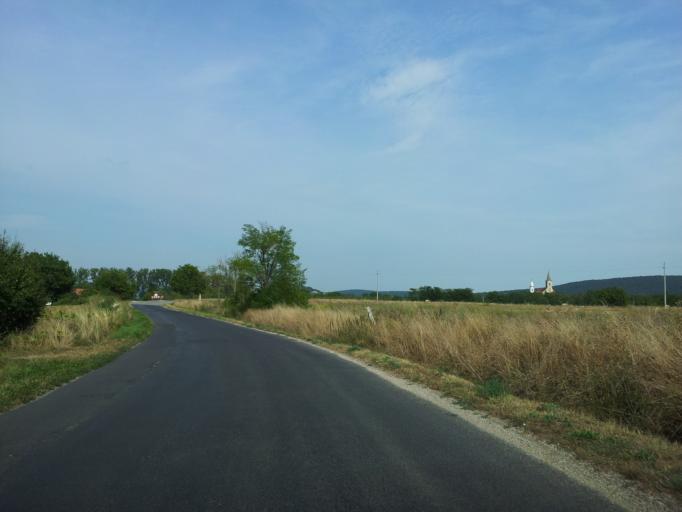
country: HU
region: Veszprem
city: Revfueloep
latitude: 46.8488
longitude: 17.5915
